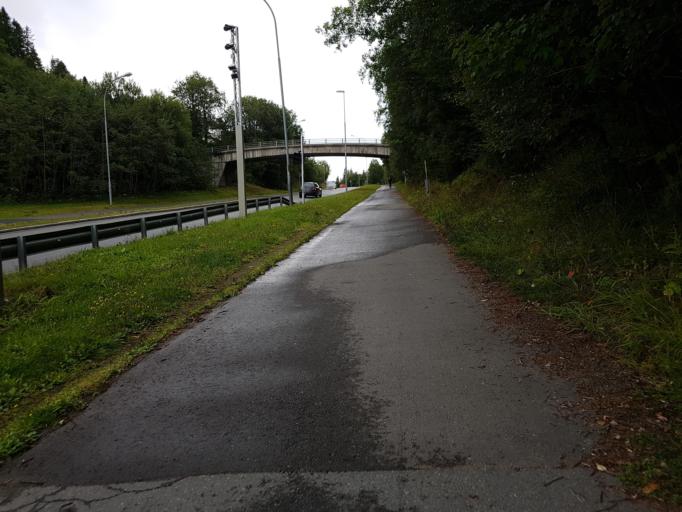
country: NO
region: Sor-Trondelag
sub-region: Trondheim
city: Trondheim
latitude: 63.4067
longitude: 10.3466
